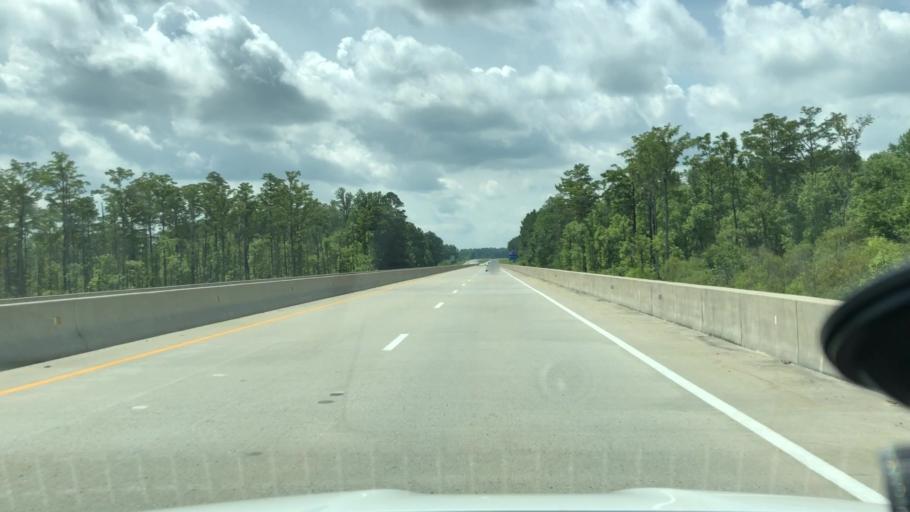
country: US
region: North Carolina
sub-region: Beaufort County
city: Washington
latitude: 35.5220
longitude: -77.0852
